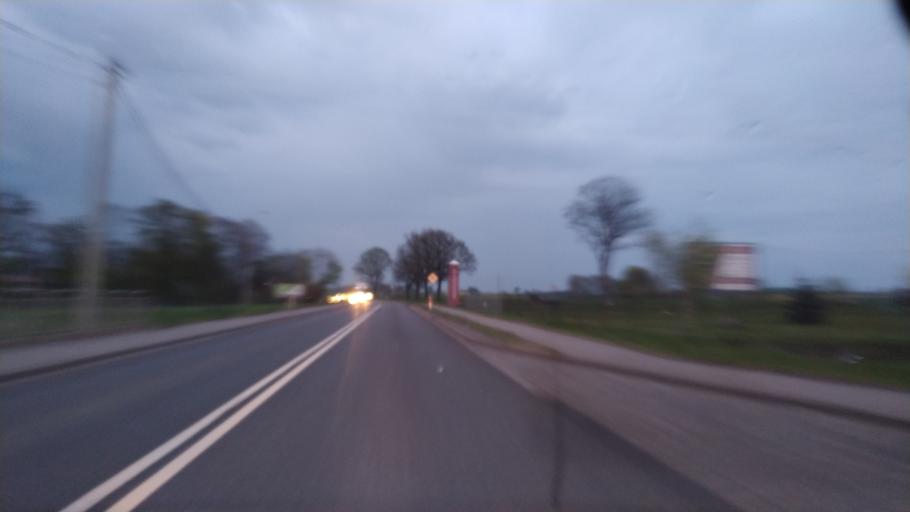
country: PL
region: West Pomeranian Voivodeship
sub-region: Powiat walecki
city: Walcz
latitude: 53.2453
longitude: 16.5522
